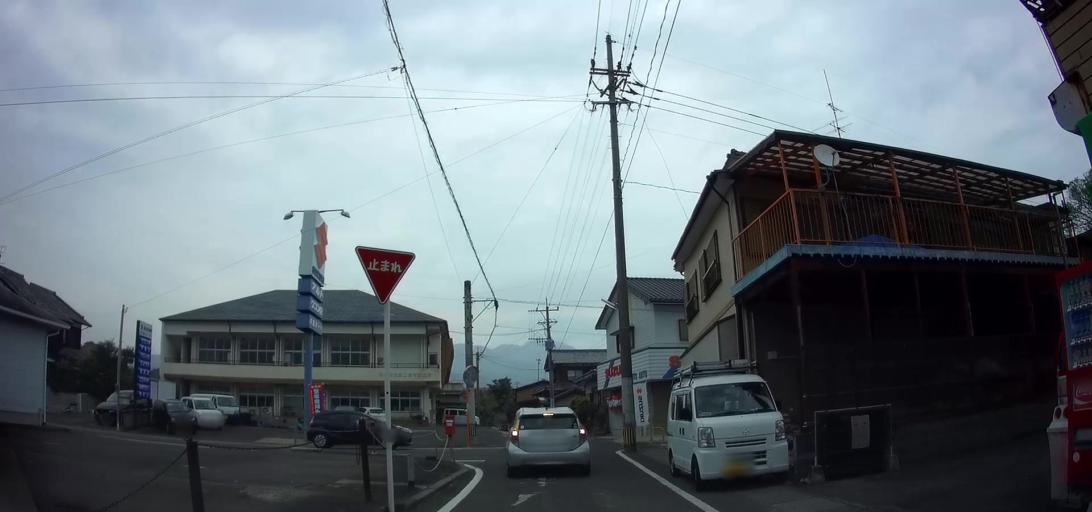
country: JP
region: Nagasaki
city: Shimabara
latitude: 32.6669
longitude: 130.3012
